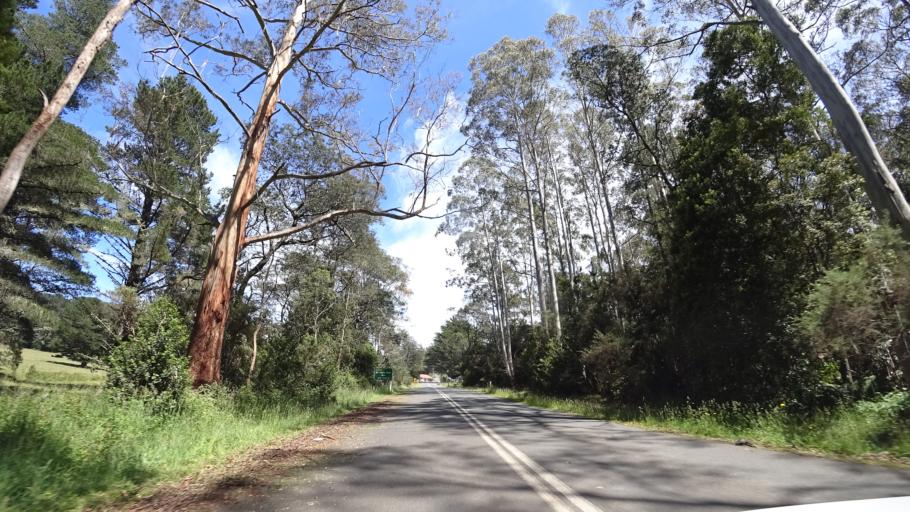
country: AU
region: Tasmania
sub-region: Break O'Day
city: St Helens
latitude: -41.1952
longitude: 147.9073
